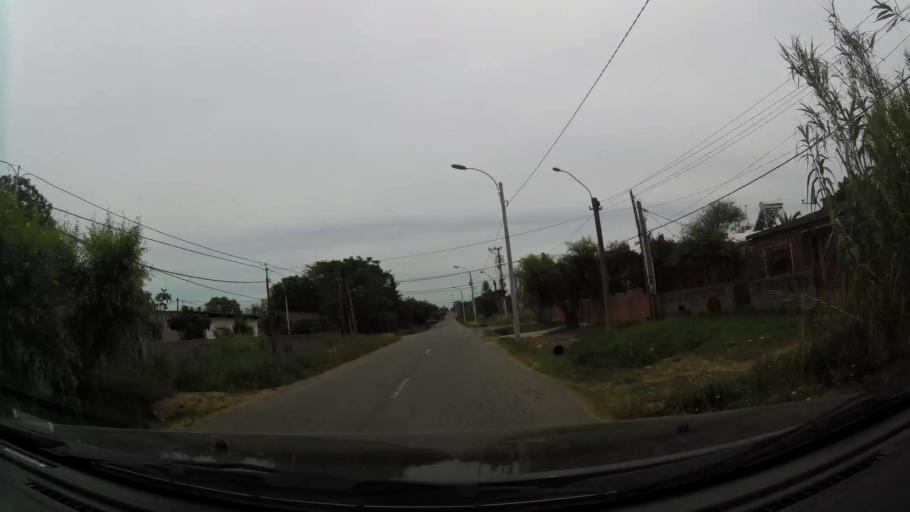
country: UY
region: Canelones
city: Las Piedras
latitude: -34.7423
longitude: -56.2315
